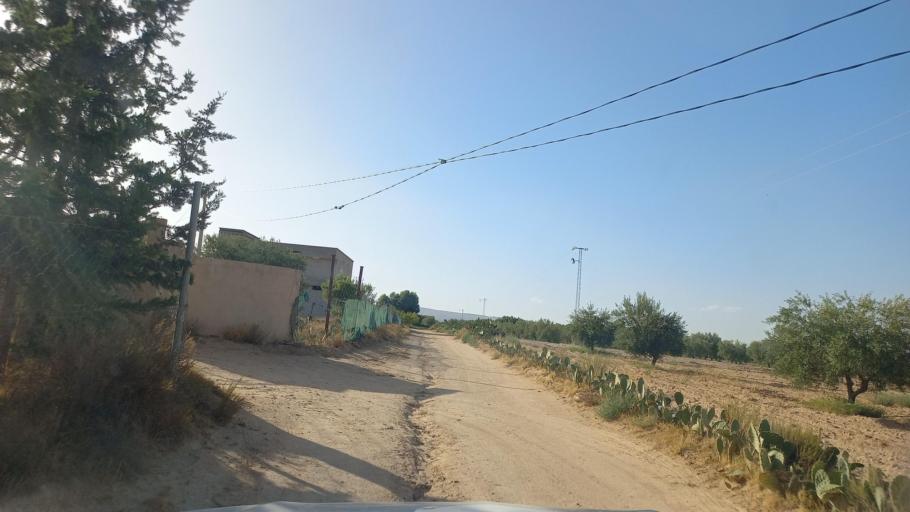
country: TN
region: Al Qasrayn
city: Kasserine
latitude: 35.2643
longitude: 9.0244
